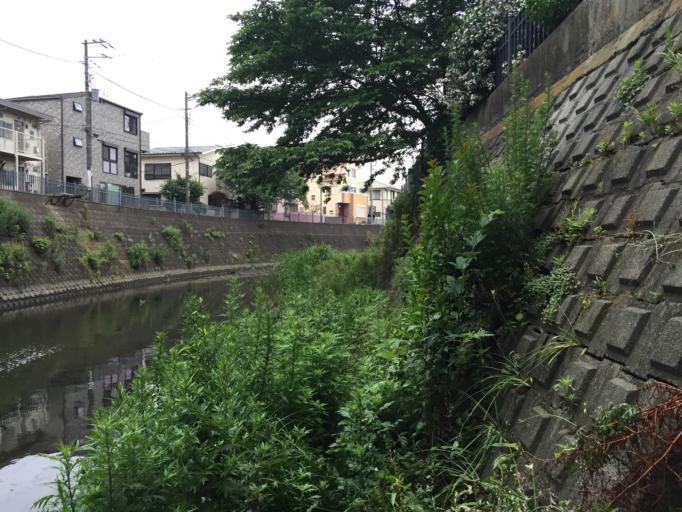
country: JP
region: Kanagawa
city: Yokohama
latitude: 35.4234
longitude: 139.6003
